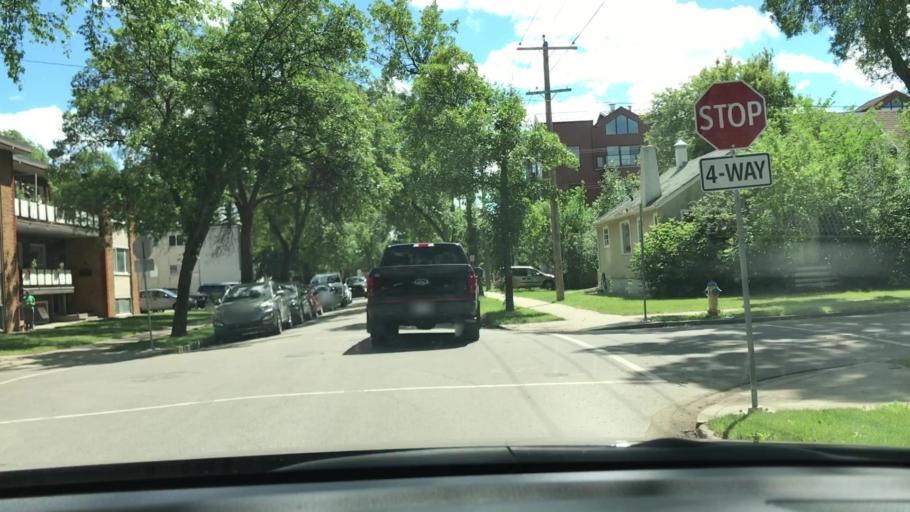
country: CA
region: Alberta
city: Edmonton
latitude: 53.5202
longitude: -113.4887
